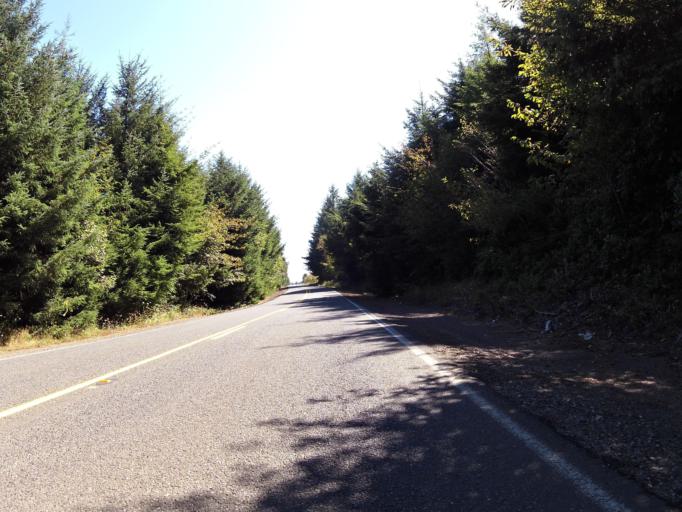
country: US
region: Oregon
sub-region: Coos County
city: Barview
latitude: 43.2636
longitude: -124.3434
